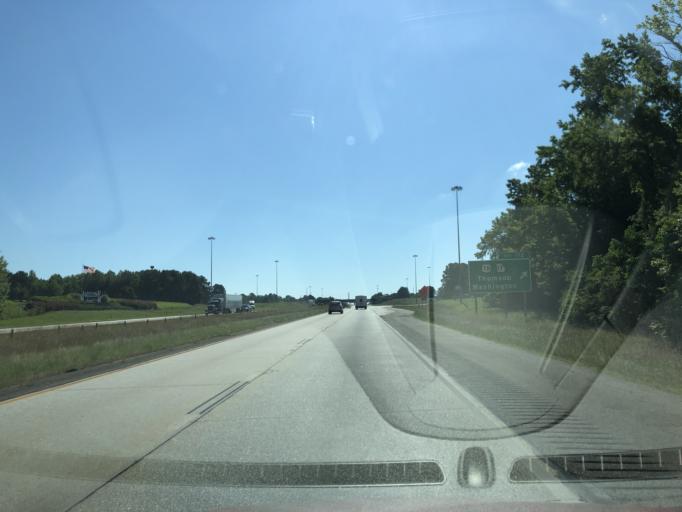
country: US
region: Georgia
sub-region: McDuffie County
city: Thomson
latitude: 33.5105
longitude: -82.5086
